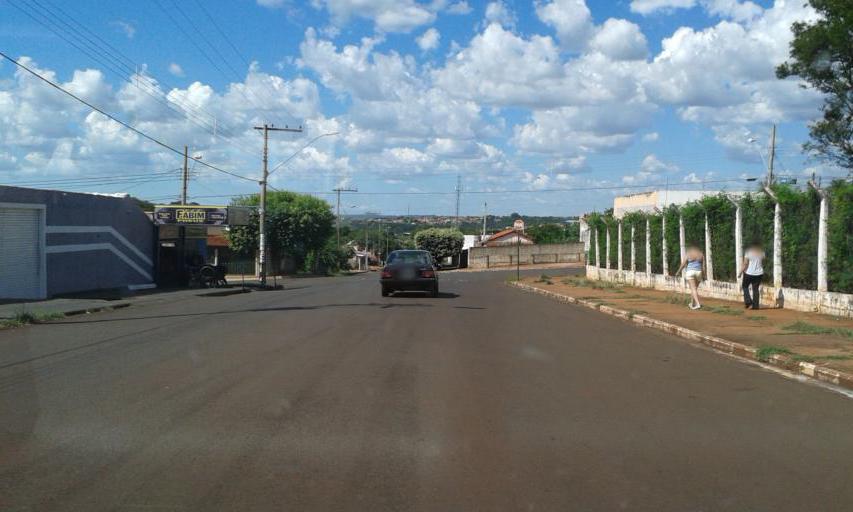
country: BR
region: Minas Gerais
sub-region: Ituiutaba
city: Ituiutaba
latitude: -18.9694
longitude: -49.4826
